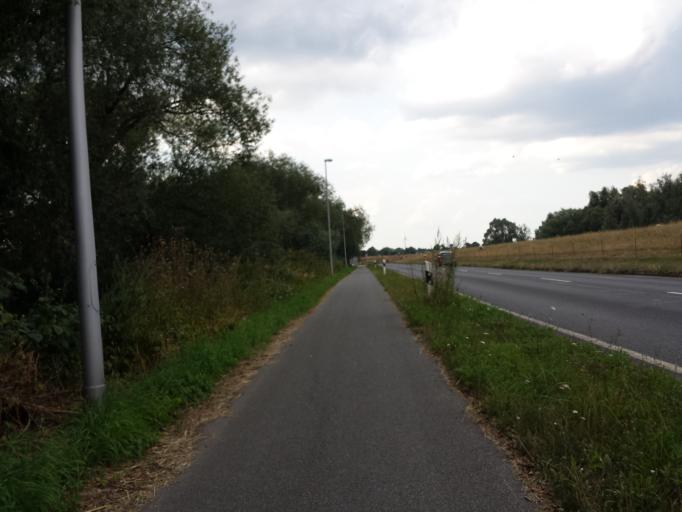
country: DE
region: Lower Saxony
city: Stuhr
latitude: 53.1035
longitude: 8.7239
